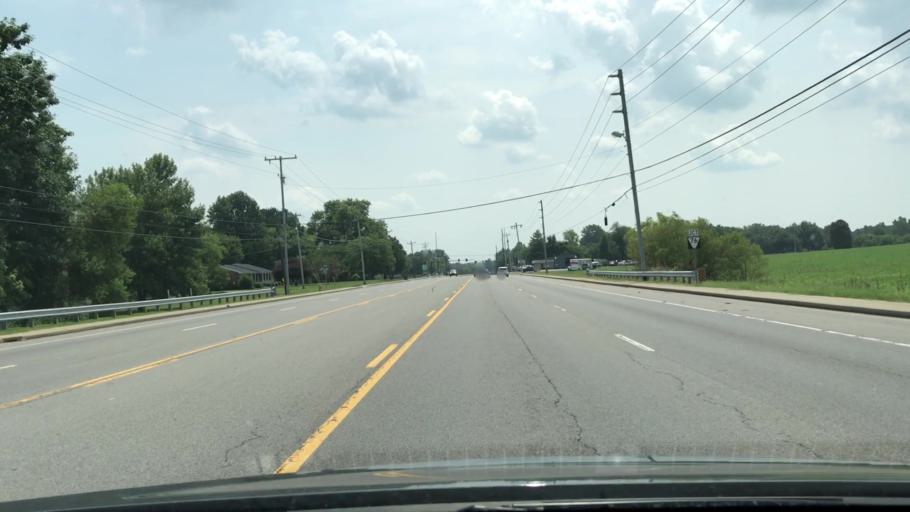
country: US
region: Tennessee
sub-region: Sumner County
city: Portland
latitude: 36.5525
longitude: -86.5074
